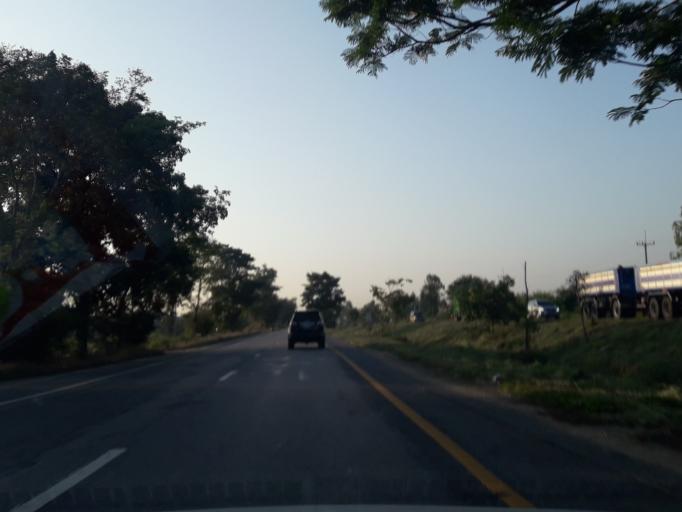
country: TH
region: Phra Nakhon Si Ayutthaya
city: Bang Pa-in
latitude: 14.2892
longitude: 100.5250
